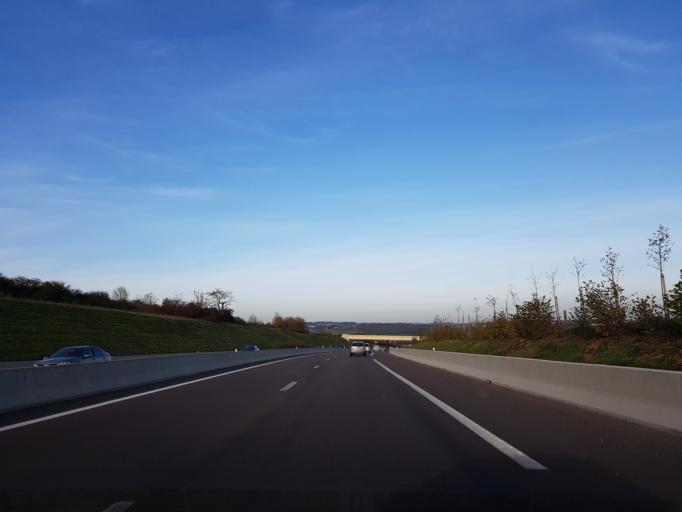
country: FR
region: Bourgogne
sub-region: Departement de la Cote-d'Or
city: Fontaine-les-Dijon
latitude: 47.3539
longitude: 5.0156
